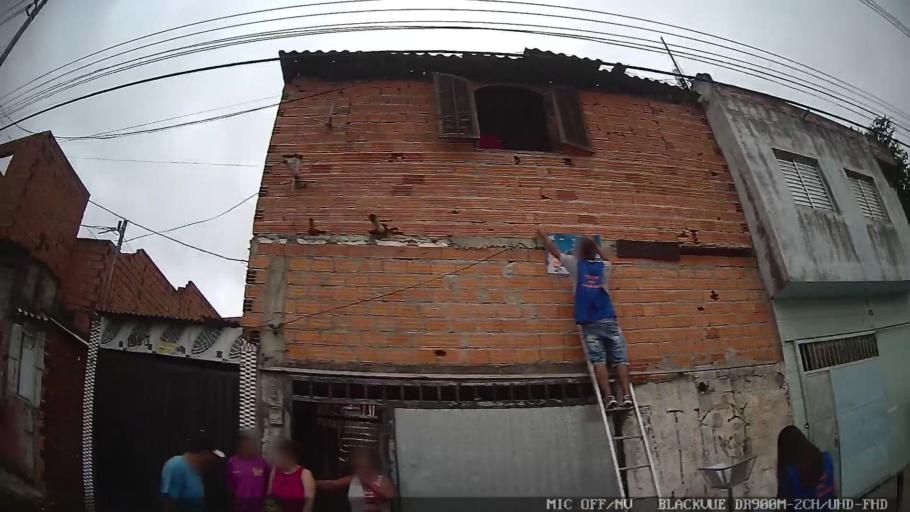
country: BR
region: Sao Paulo
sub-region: Itaquaquecetuba
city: Itaquaquecetuba
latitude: -23.4719
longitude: -46.4014
